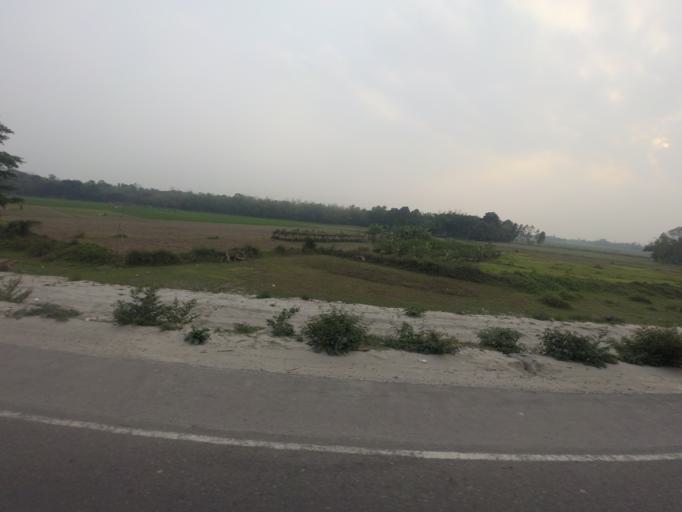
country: BD
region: Dhaka
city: Tangail
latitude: 24.1801
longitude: 90.0079
